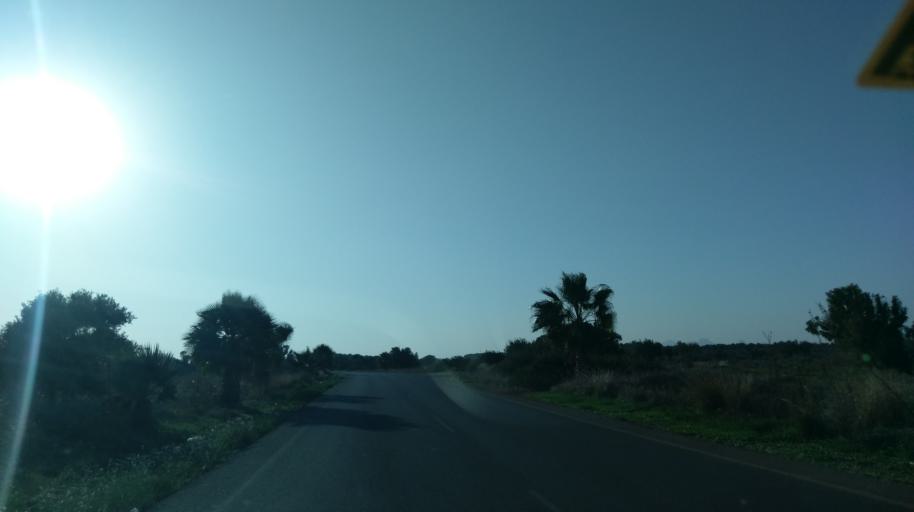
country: CY
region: Ammochostos
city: Leonarisso
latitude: 35.3805
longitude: 34.0625
